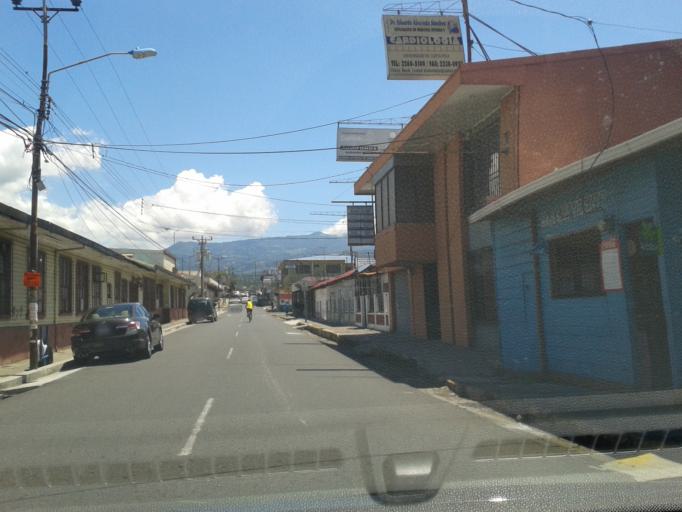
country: CR
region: Heredia
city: San Francisco
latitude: 9.9953
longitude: -84.1226
